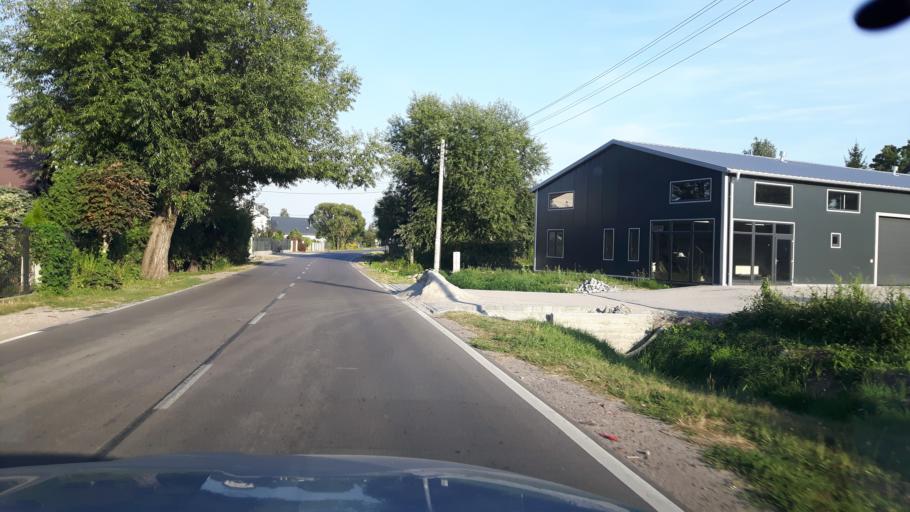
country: PL
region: Masovian Voivodeship
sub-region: Powiat wolominski
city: Slupno
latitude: 52.3612
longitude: 21.1686
